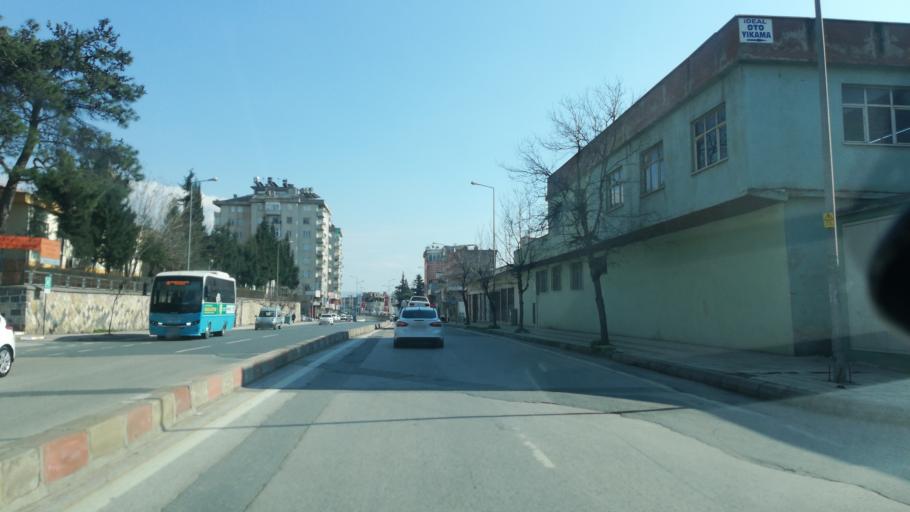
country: TR
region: Kahramanmaras
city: Kahramanmaras
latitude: 37.5732
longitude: 36.9393
